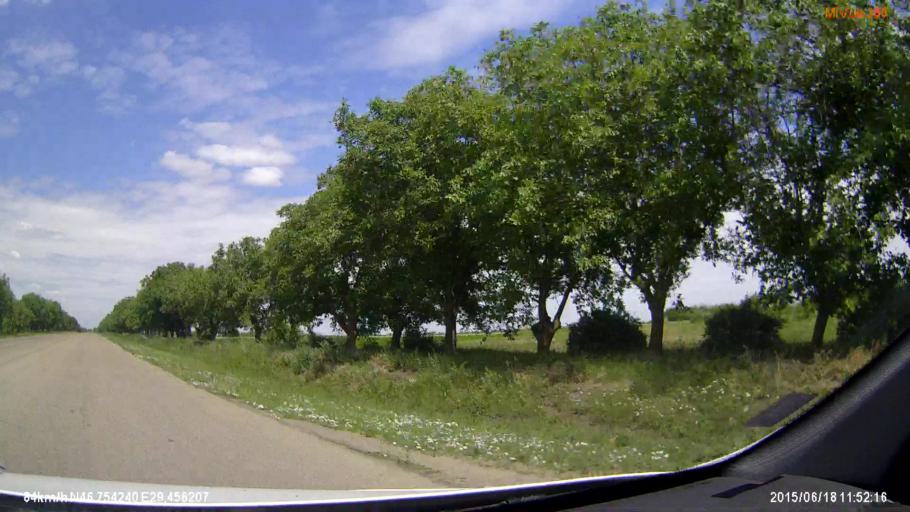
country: MD
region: Bender
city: Bender
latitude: 46.7538
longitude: 29.4561
